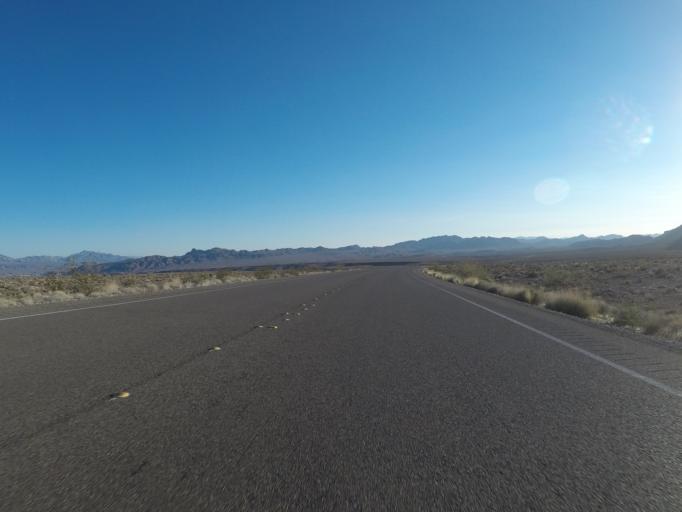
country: US
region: Nevada
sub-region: Clark County
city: Moapa Valley
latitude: 36.3550
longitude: -114.4827
